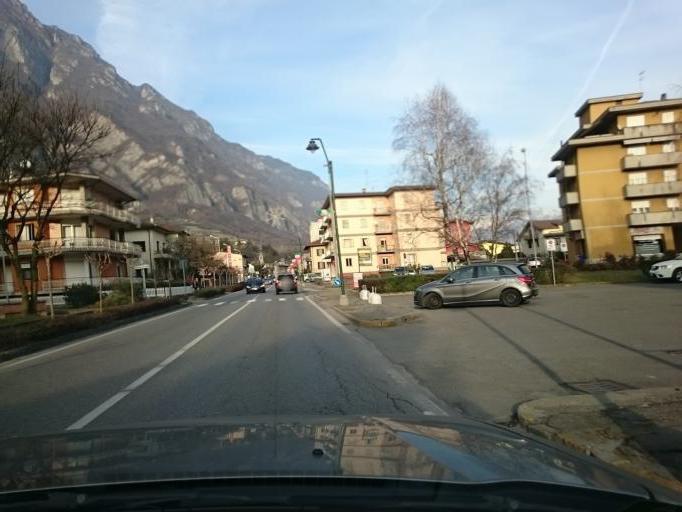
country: IT
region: Lombardy
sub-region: Provincia di Brescia
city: Darfo Boario Terme
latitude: 45.8969
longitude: 10.1915
